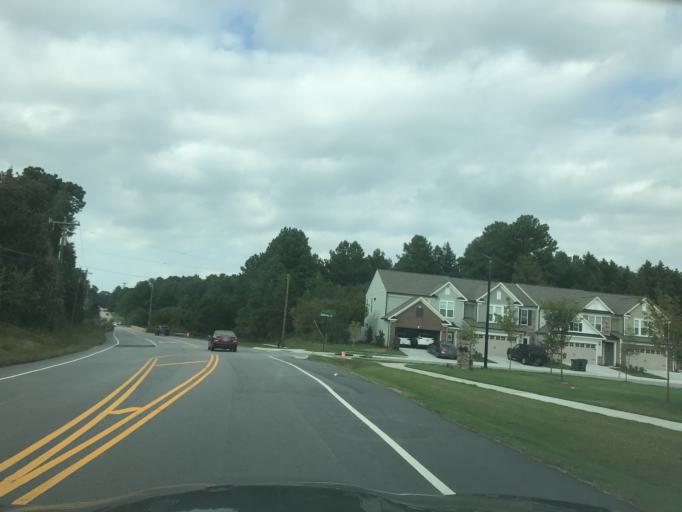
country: US
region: North Carolina
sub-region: Durham County
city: Durham
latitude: 35.9071
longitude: -78.9163
